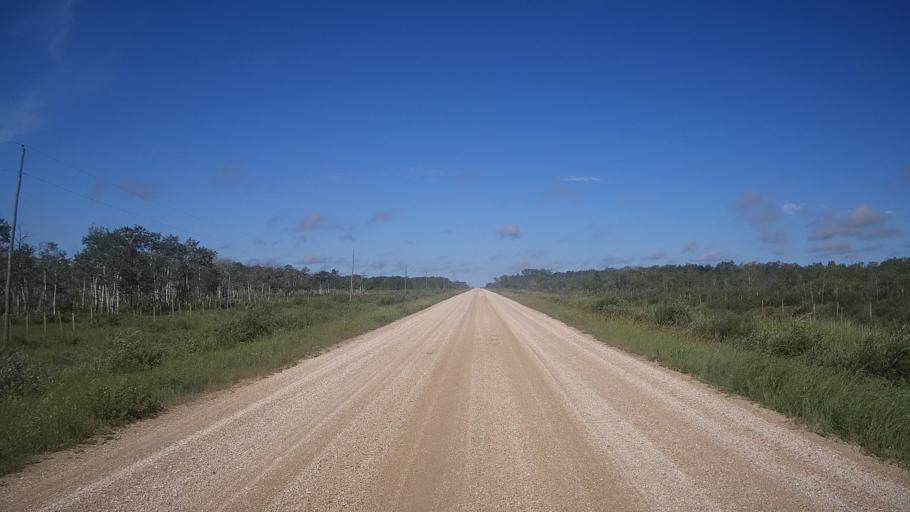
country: CA
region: Manitoba
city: Stonewall
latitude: 50.2411
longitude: -97.7531
